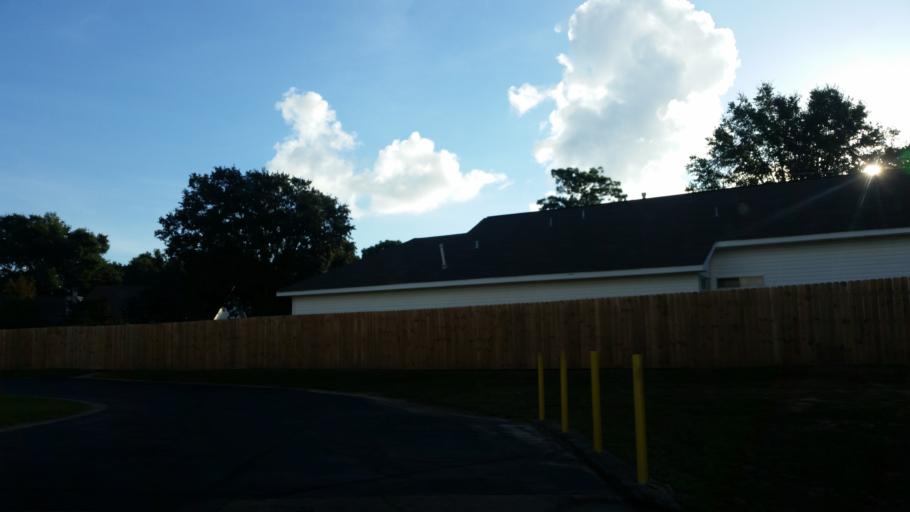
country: US
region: Florida
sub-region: Escambia County
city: Ferry Pass
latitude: 30.5104
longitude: -87.1825
